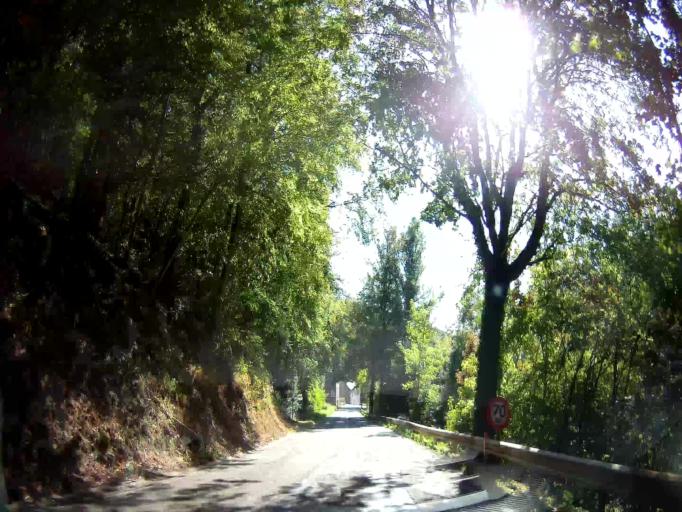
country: BE
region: Wallonia
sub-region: Province de Namur
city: Houyet
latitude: 50.2228
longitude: 4.9872
